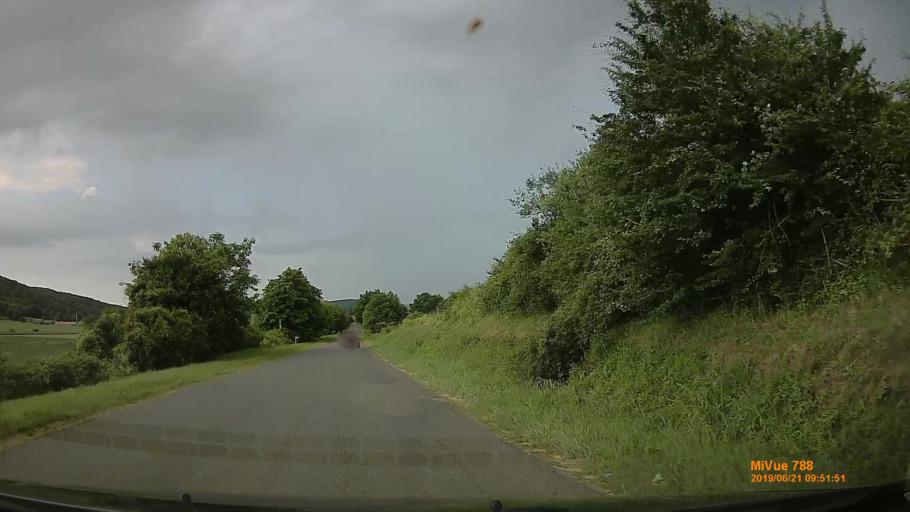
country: HU
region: Baranya
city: Sasd
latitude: 46.2479
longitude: 18.0199
